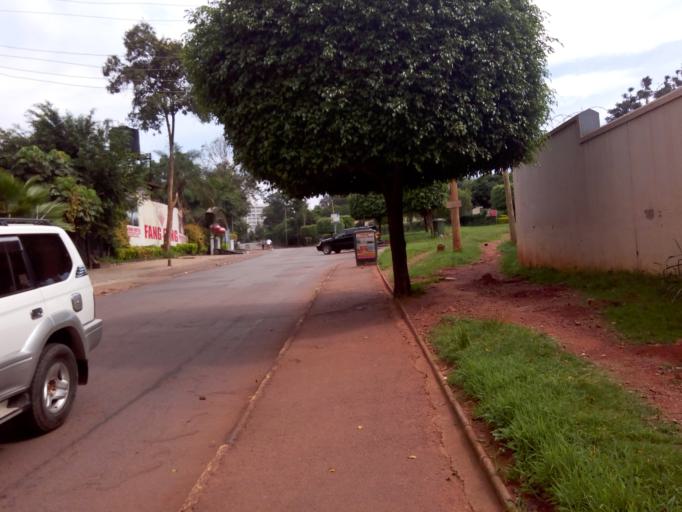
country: UG
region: Central Region
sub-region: Kampala District
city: Kampala
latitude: 0.3213
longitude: 32.5843
